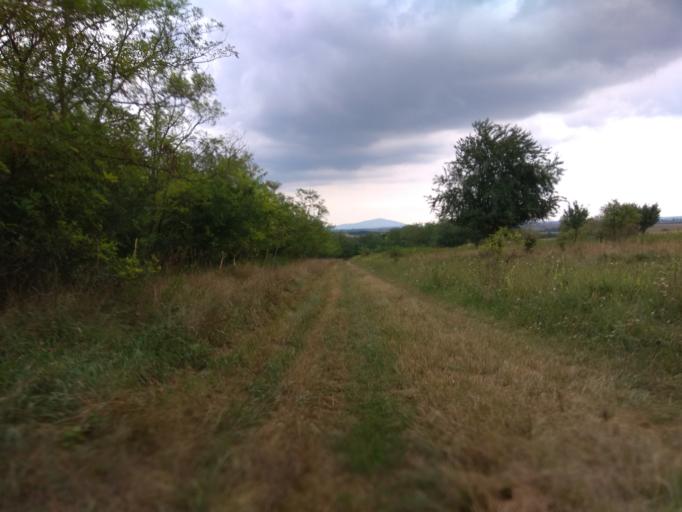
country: HU
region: Borsod-Abauj-Zemplen
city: Megyaszo
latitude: 48.1457
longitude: 21.0700
